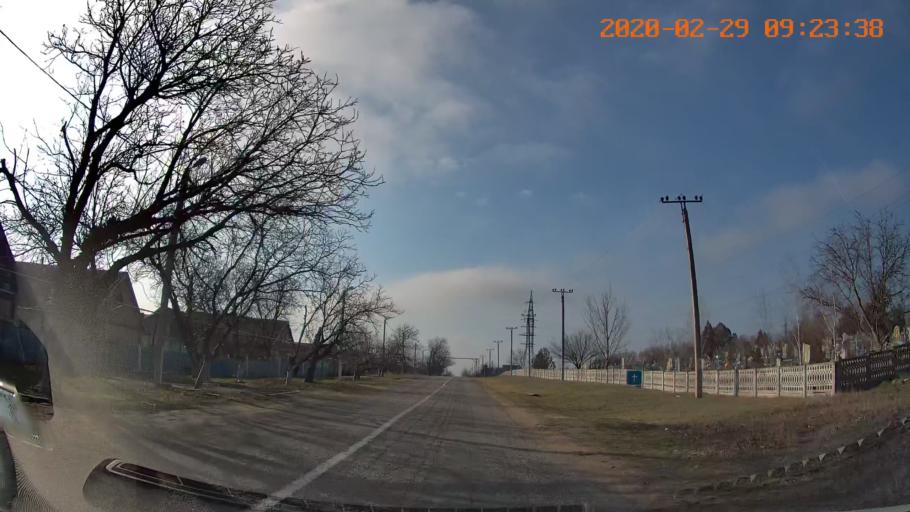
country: MD
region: Telenesti
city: Pervomaisc
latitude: 46.7238
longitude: 29.9607
